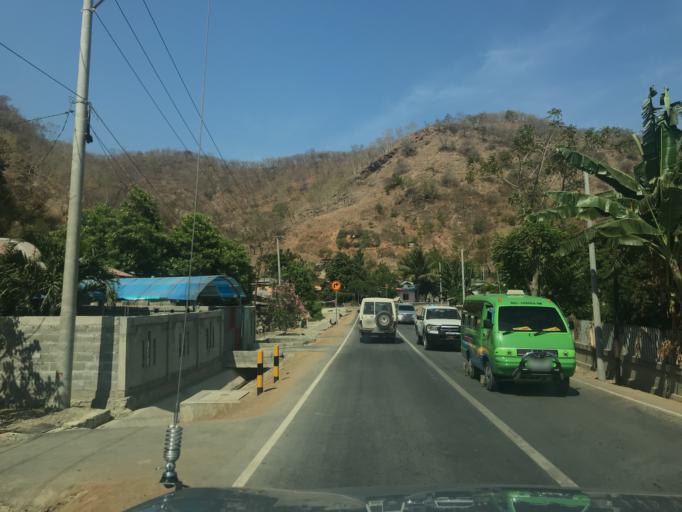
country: TL
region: Dili
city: Dili
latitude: -8.5583
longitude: 125.5218
